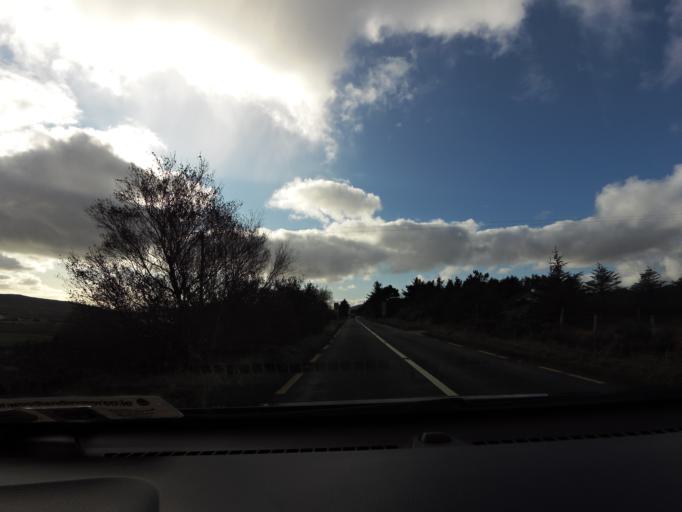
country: IE
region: Connaught
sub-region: Maigh Eo
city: Belmullet
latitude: 53.9405
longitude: -9.8969
